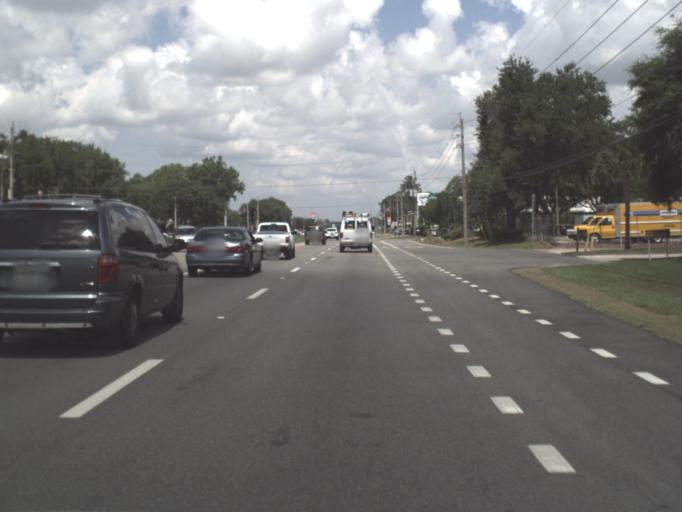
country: US
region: Florida
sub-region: Saint Johns County
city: Fruit Cove
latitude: 30.1730
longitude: -81.5462
